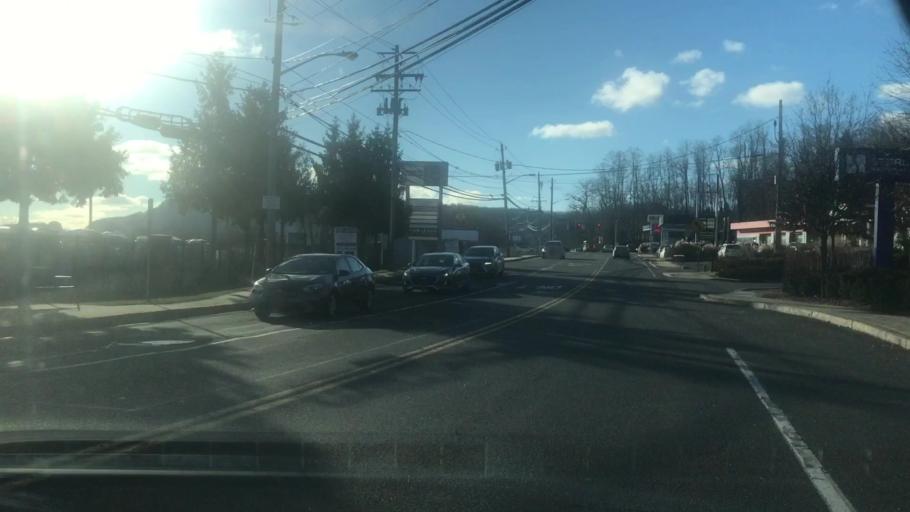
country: US
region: New York
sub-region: Rockland County
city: West Haverstraw
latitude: 41.2180
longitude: -73.9865
